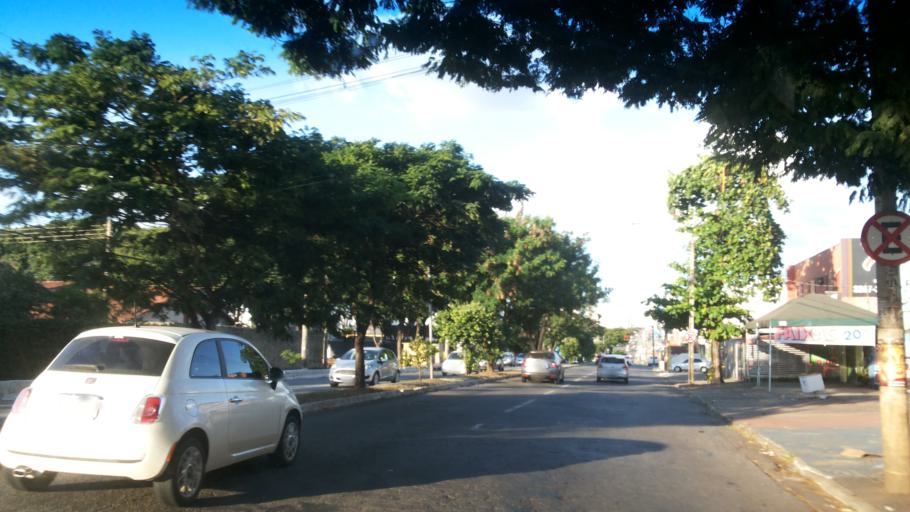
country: BR
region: Goias
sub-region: Goiania
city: Goiania
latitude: -16.7110
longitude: -49.2994
